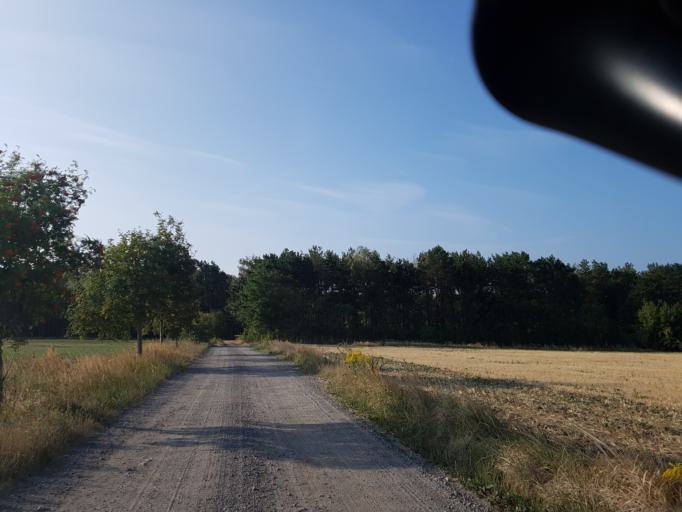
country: DE
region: Brandenburg
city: Niemegk
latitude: 52.0769
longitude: 12.7160
